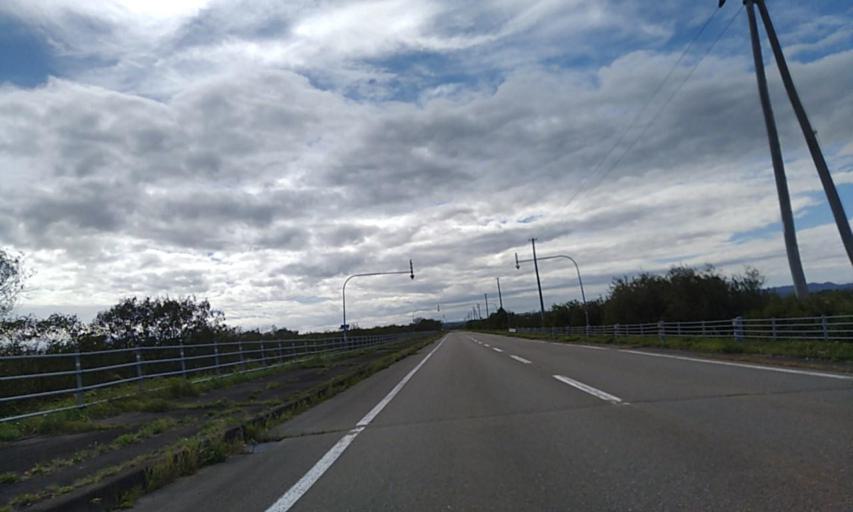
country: JP
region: Hokkaido
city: Obihiro
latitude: 42.7249
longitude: 143.6686
